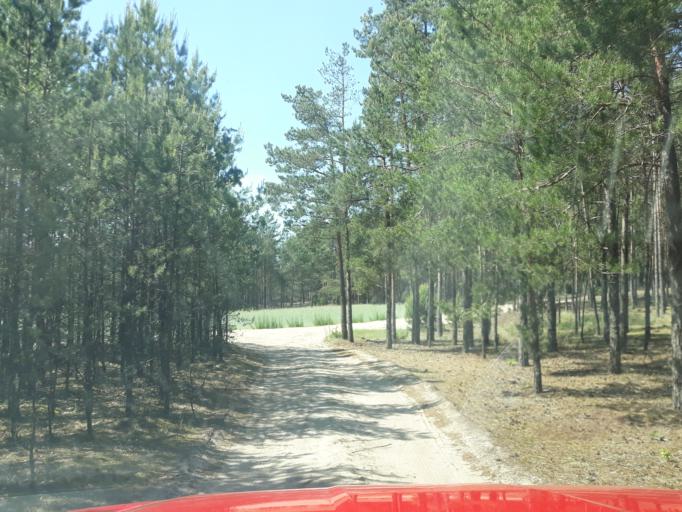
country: PL
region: Pomeranian Voivodeship
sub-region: Powiat chojnicki
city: Chojnice
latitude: 53.8680
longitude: 17.5433
